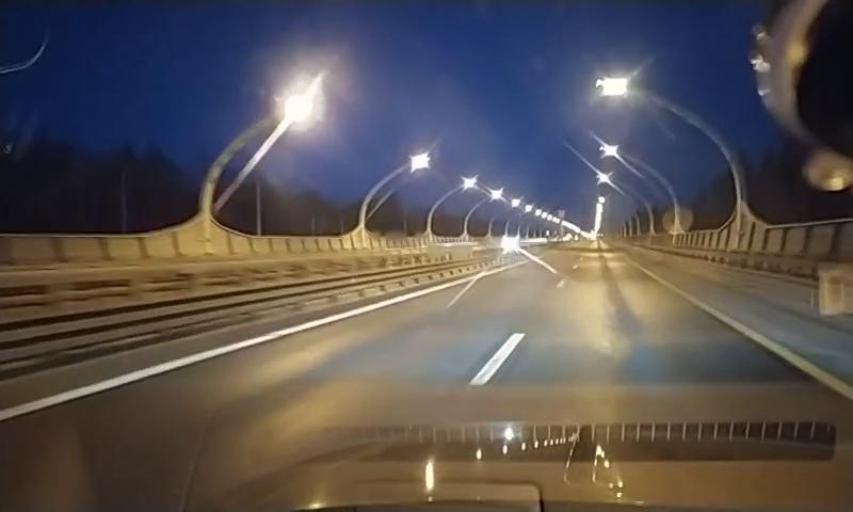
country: RU
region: St.-Petersburg
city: Beloostrov
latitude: 60.1390
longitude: 30.0449
